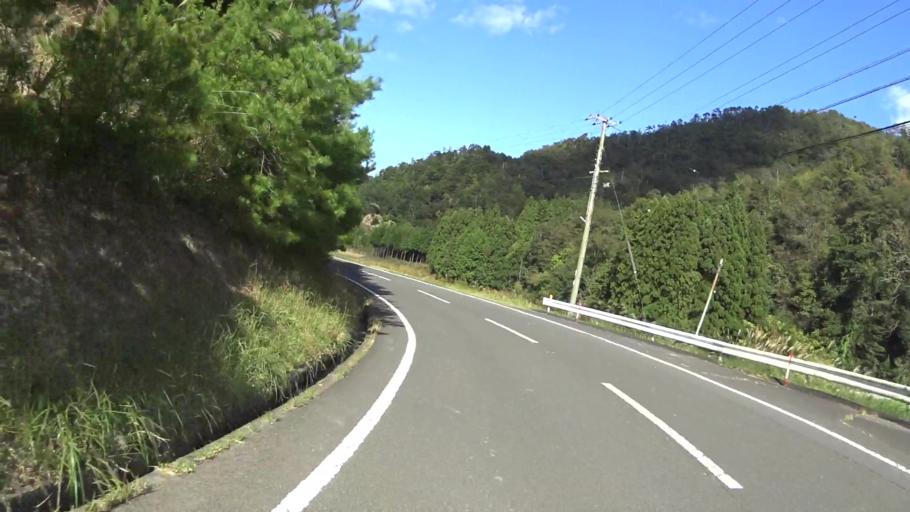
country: JP
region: Kyoto
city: Miyazu
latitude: 35.5708
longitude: 135.0171
